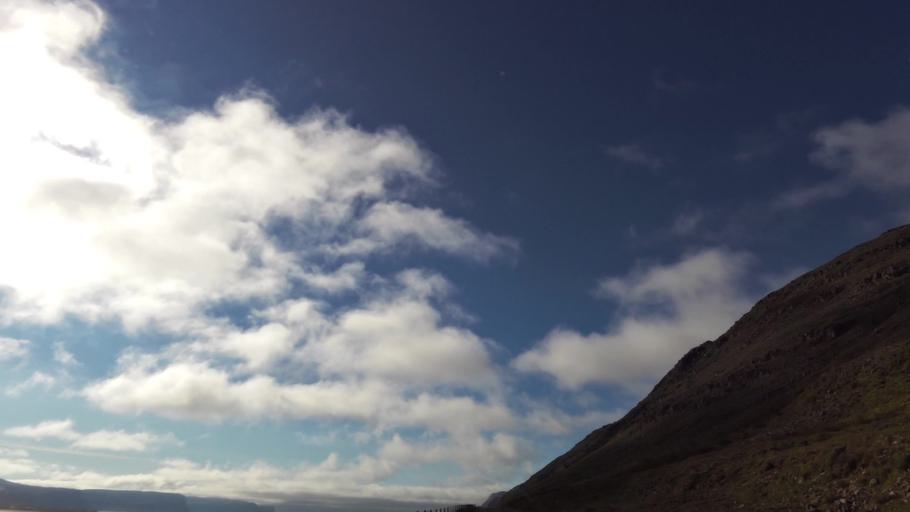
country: IS
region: West
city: Olafsvik
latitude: 65.5531
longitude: -23.8938
